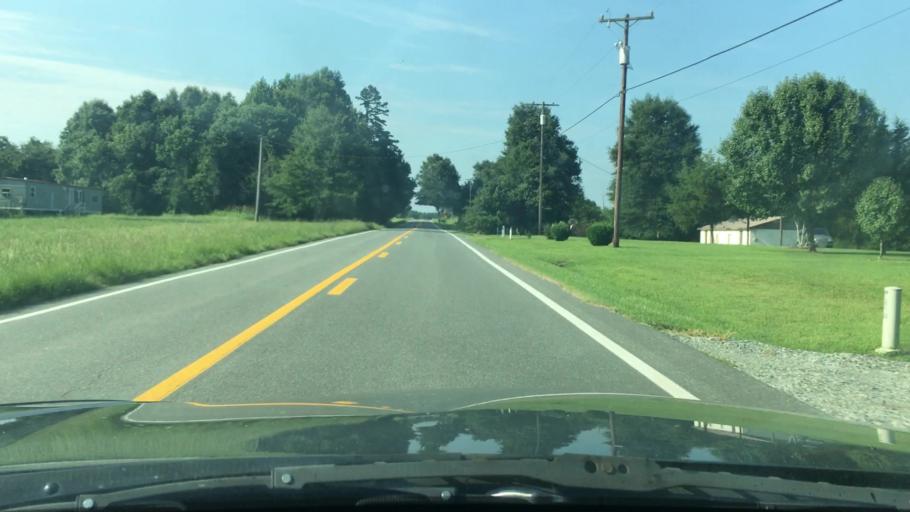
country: US
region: North Carolina
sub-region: Alamance County
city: Green Level
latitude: 36.2300
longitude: -79.3224
